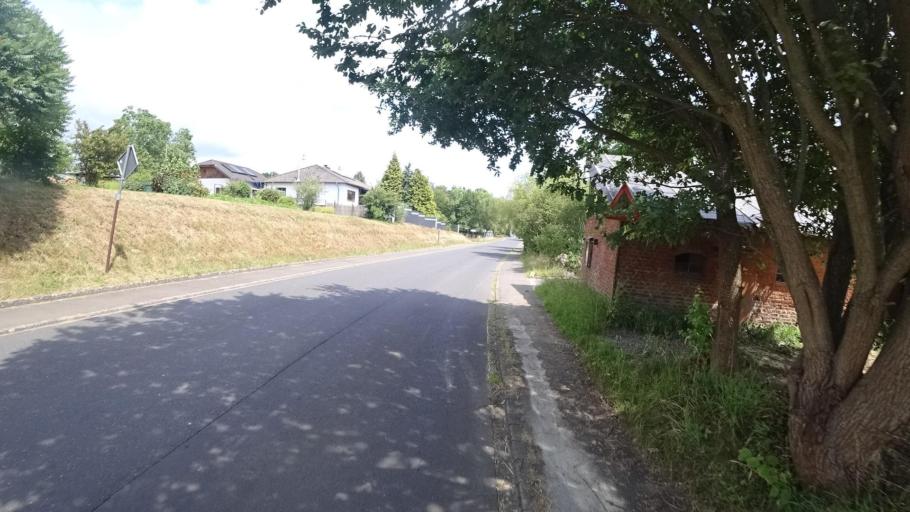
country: DE
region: Rheinland-Pfalz
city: Oberirsen
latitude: 50.7218
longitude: 7.5689
